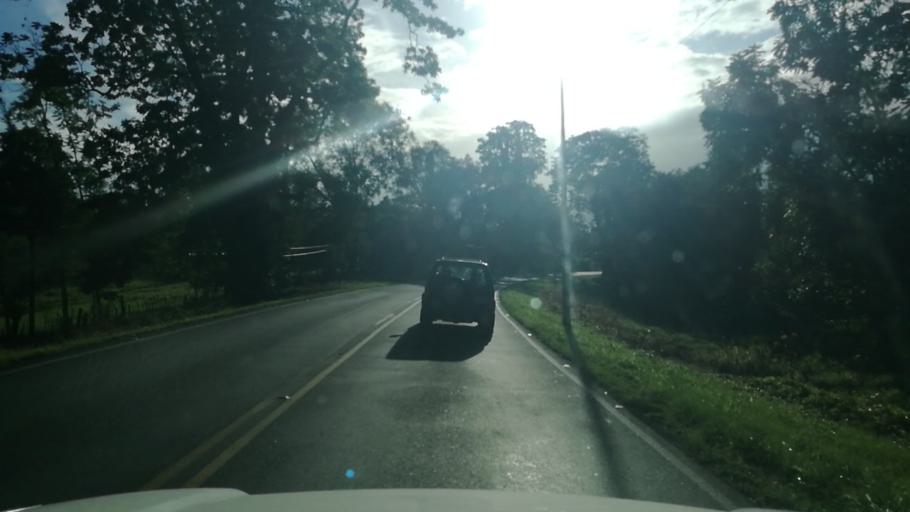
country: CR
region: Limon
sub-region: Canton de Matina
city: Batan
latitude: 10.0550
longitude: -83.3621
